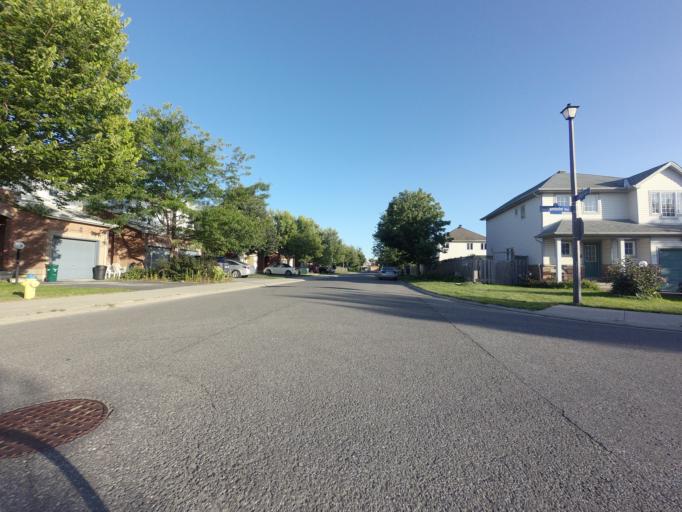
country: CA
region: Ontario
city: Bells Corners
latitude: 45.2844
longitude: -75.7340
